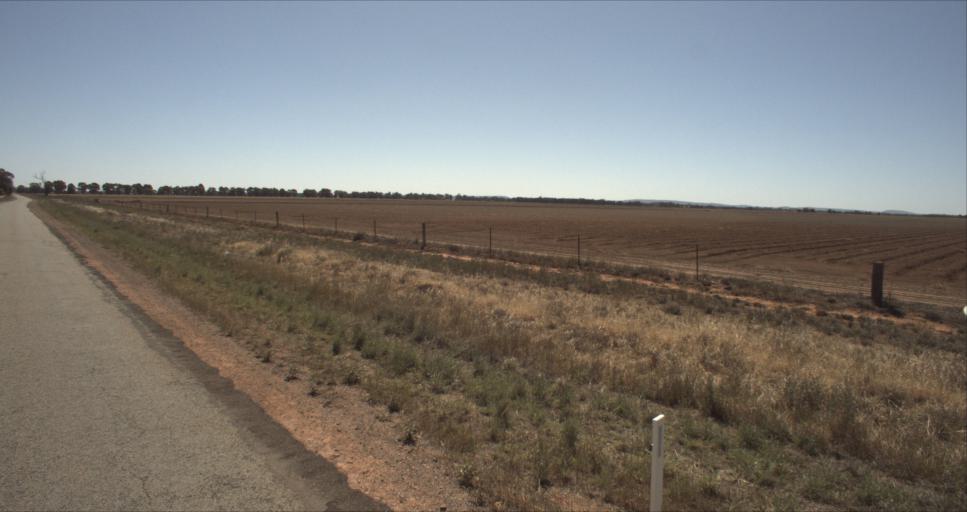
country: AU
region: New South Wales
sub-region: Leeton
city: Leeton
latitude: -34.5592
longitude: 146.3130
